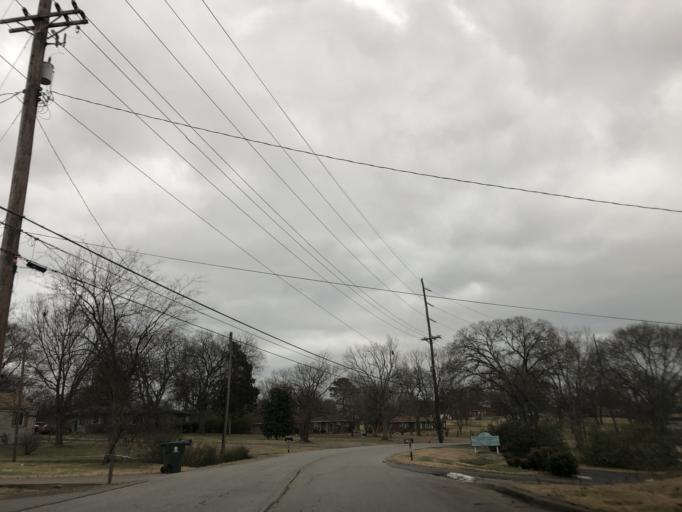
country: US
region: Tennessee
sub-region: Davidson County
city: Goodlettsville
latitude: 36.2972
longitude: -86.6937
